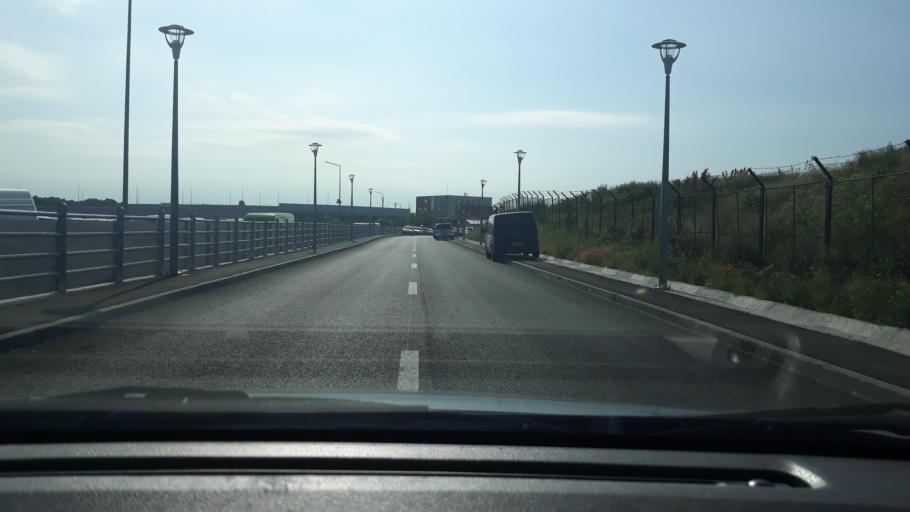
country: RO
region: Bihor
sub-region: Comuna Biharea
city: Oradea
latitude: 47.0390
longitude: 21.9079
